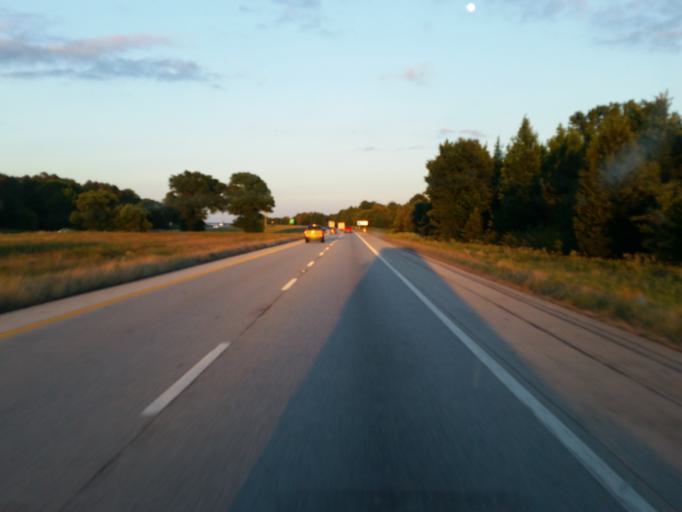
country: US
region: Texas
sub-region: Smith County
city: Hideaway
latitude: 32.4857
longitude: -95.5354
